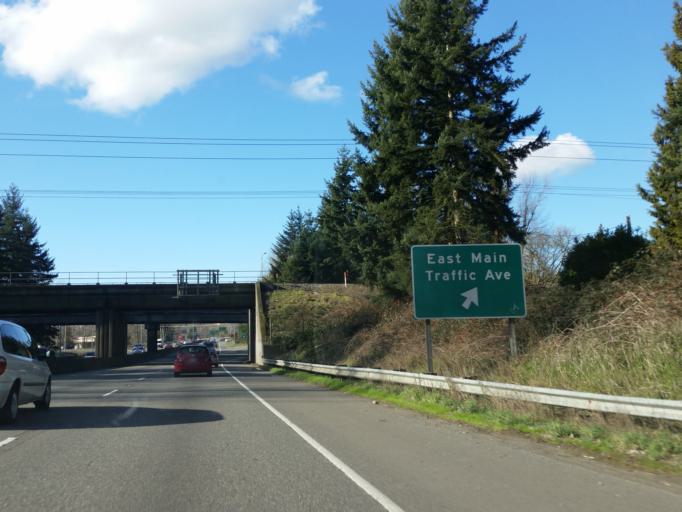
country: US
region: Washington
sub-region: Pierce County
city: Sumner
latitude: 47.1974
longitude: -122.2479
